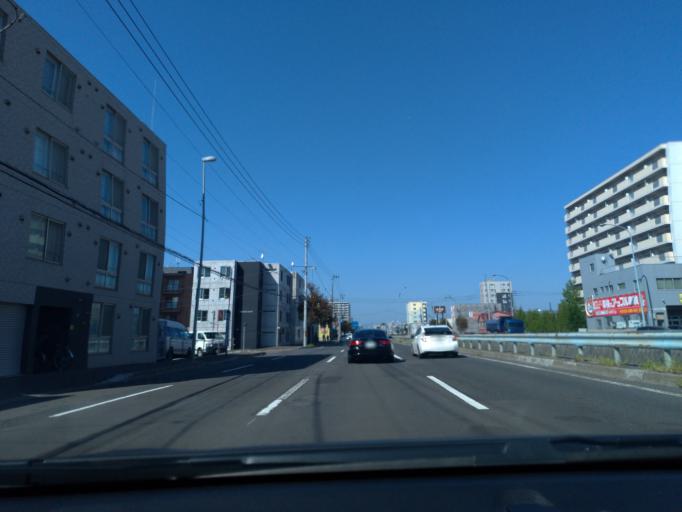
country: JP
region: Hokkaido
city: Sapporo
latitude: 43.0866
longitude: 141.3487
